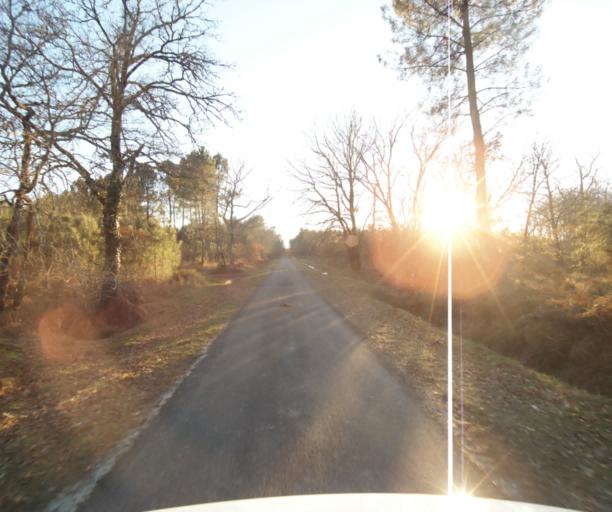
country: FR
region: Aquitaine
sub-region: Departement des Landes
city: Gabarret
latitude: 44.1189
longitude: -0.0238
